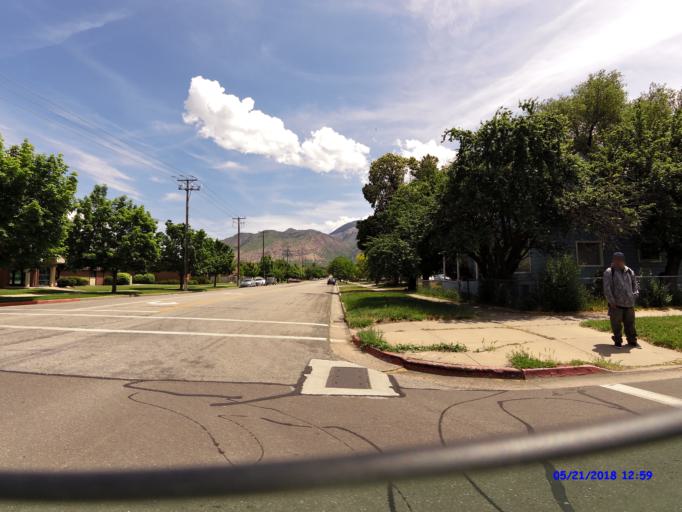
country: US
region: Utah
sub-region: Weber County
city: Ogden
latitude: 41.2164
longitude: -111.9762
